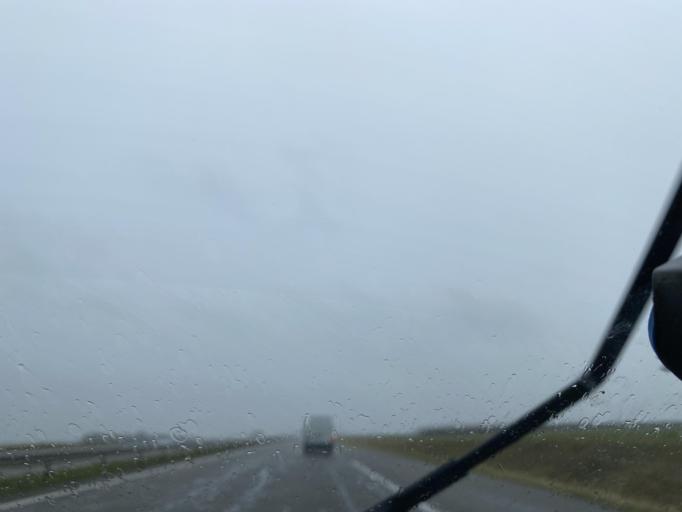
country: FR
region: Centre
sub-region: Departement d'Eure-et-Loir
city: Villemeux-sur-Eure
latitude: 48.6365
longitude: 1.4093
